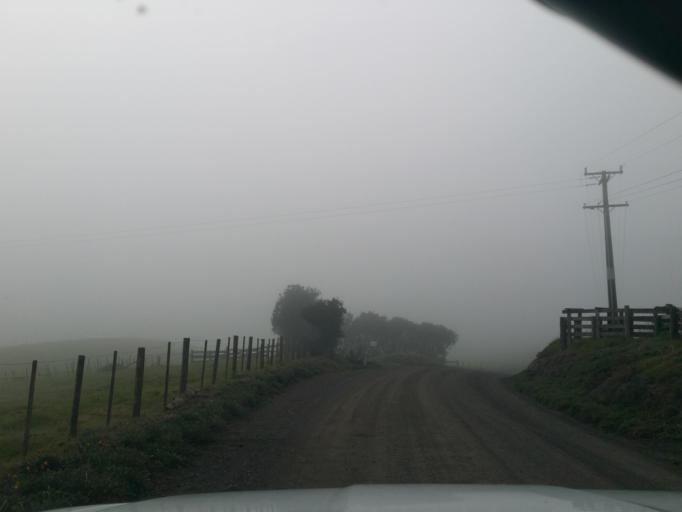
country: NZ
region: Northland
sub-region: Kaipara District
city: Dargaville
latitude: -35.9102
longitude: 173.7750
